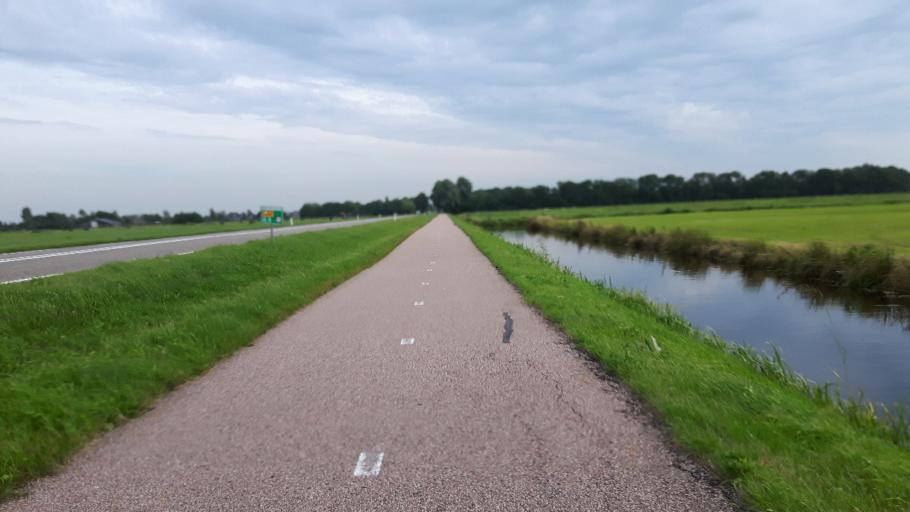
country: NL
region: Utrecht
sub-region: Gemeente Woerden
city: Woerden
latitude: 52.1372
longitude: 4.9118
